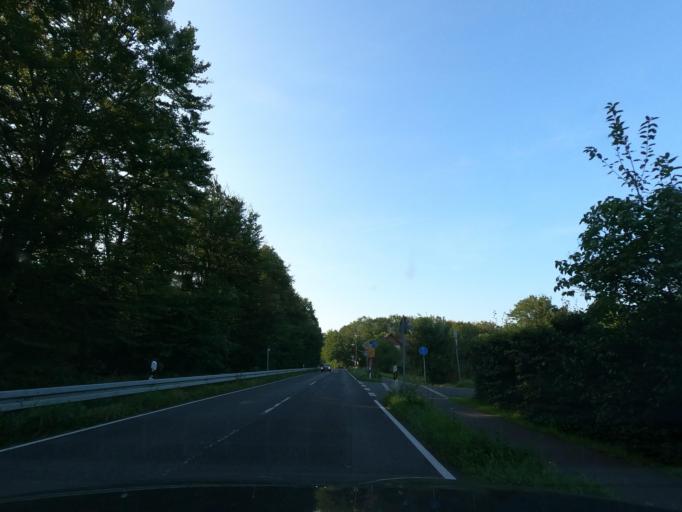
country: DE
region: North Rhine-Westphalia
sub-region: Regierungsbezirk Dusseldorf
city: Hunxe
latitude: 51.5940
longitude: 6.8145
